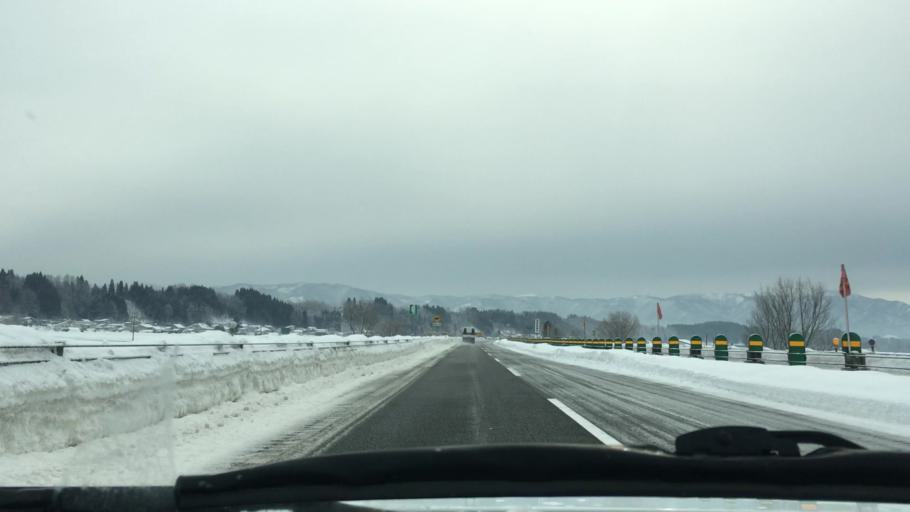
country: JP
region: Akita
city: Hanawa
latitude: 40.3002
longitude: 140.7475
